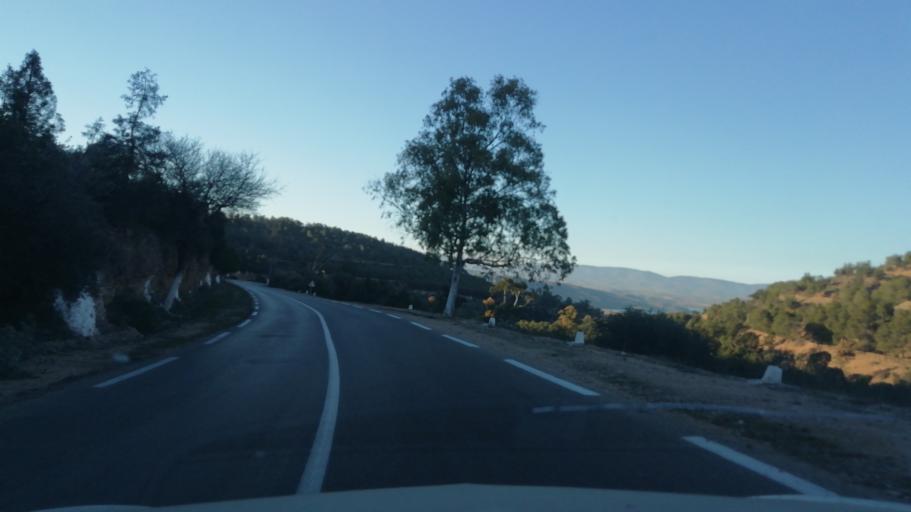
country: DZ
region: Tlemcen
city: Beni Mester
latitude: 34.8160
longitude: -1.6329
